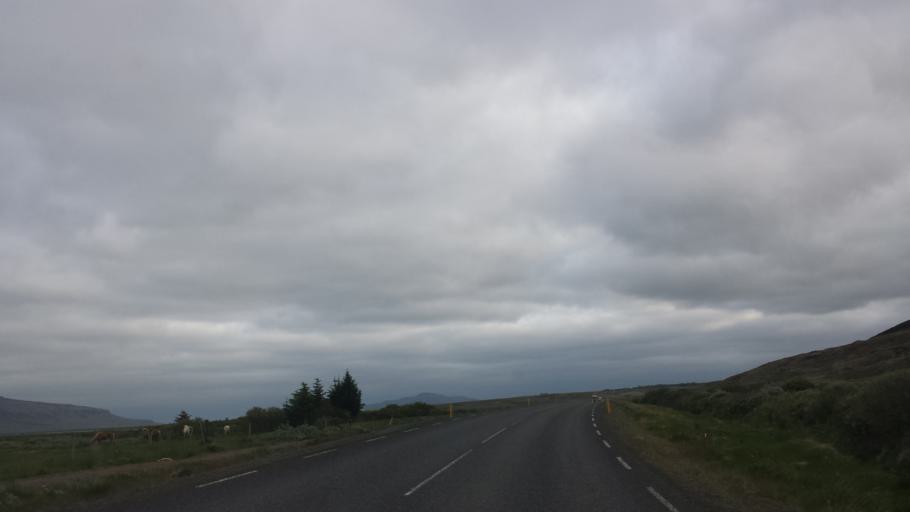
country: IS
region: South
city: Selfoss
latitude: 64.1368
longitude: -20.5747
